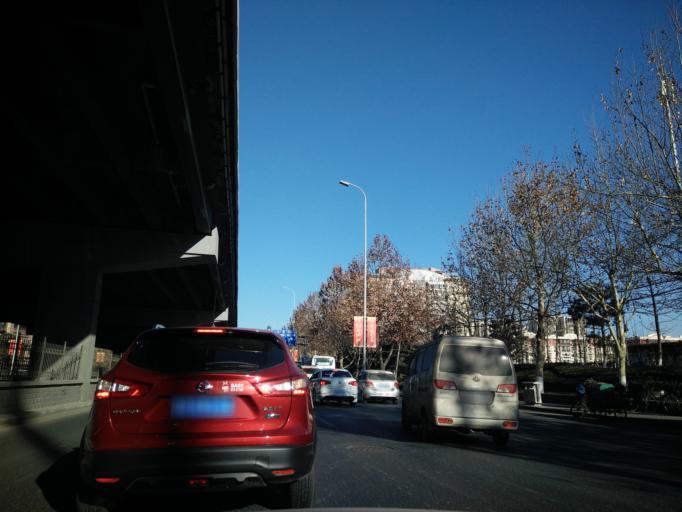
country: CN
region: Beijing
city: Xingfeng
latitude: 39.7357
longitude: 116.3395
